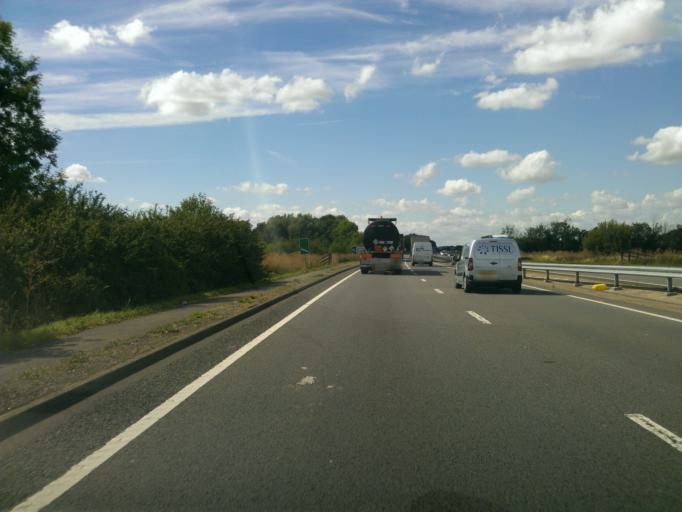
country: GB
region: England
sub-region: Cambridgeshire
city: Buckden
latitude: 52.3389
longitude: -0.3320
